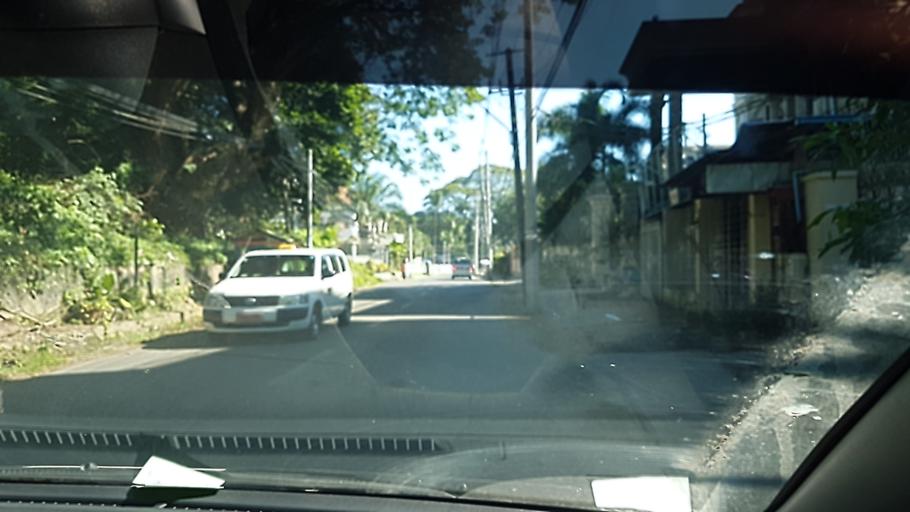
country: MM
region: Yangon
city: Yangon
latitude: 16.8171
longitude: 96.1512
